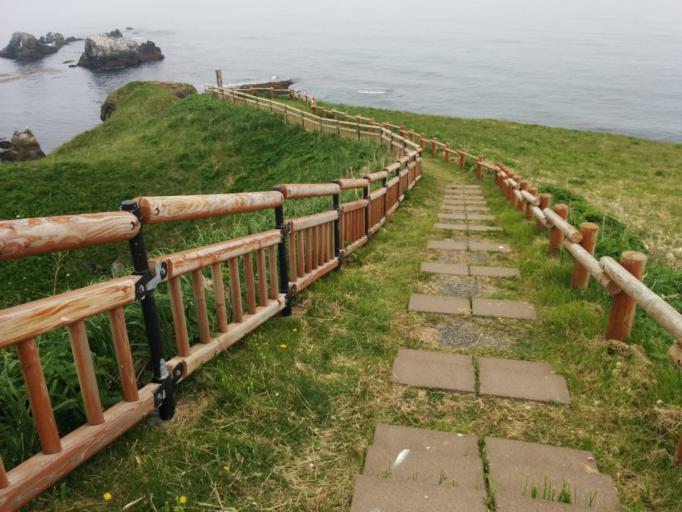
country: JP
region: Hokkaido
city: Nemuro
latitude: 43.0766
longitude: 145.1705
